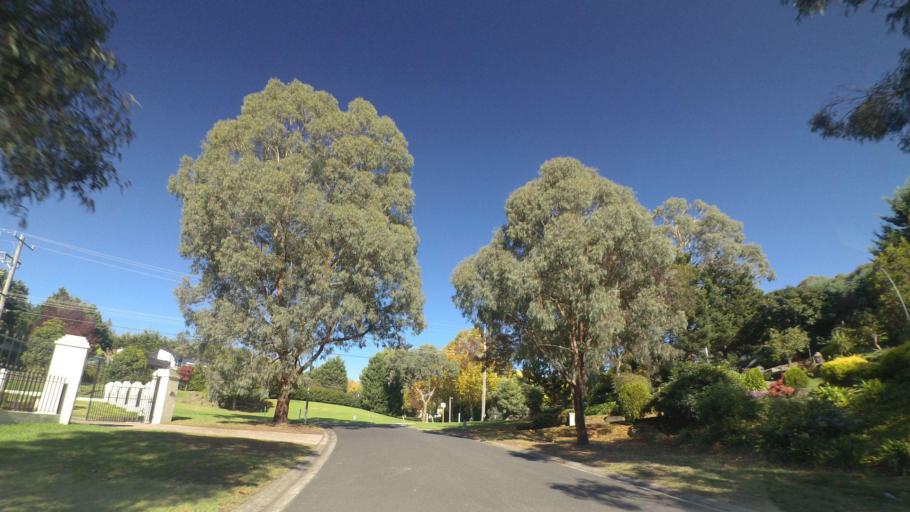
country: AU
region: Victoria
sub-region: Nillumbik
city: Eltham
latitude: -37.7479
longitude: 145.1625
